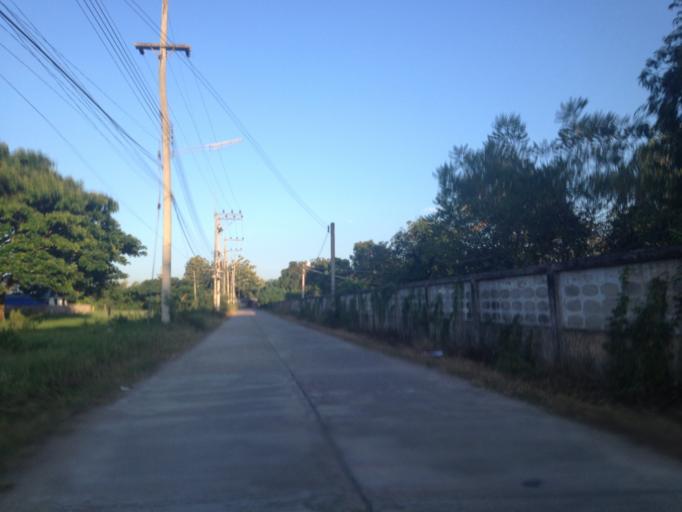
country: TH
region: Chiang Mai
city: Hang Dong
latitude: 18.6777
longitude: 98.9121
